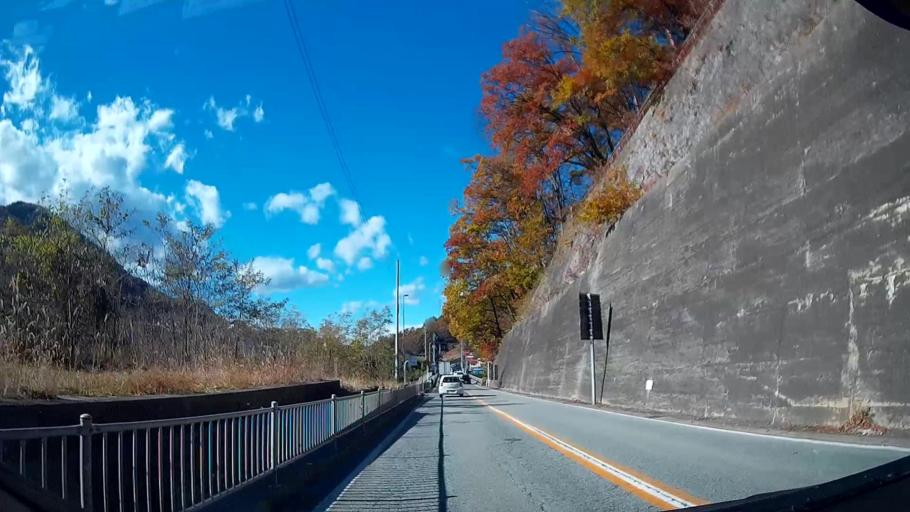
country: JP
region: Yamanashi
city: Enzan
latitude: 35.6409
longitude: 138.7747
